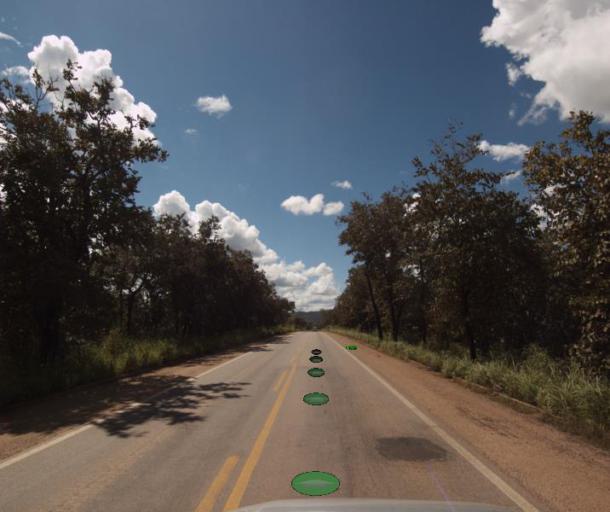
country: BR
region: Goias
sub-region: Porangatu
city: Porangatu
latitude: -13.6849
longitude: -49.0231
